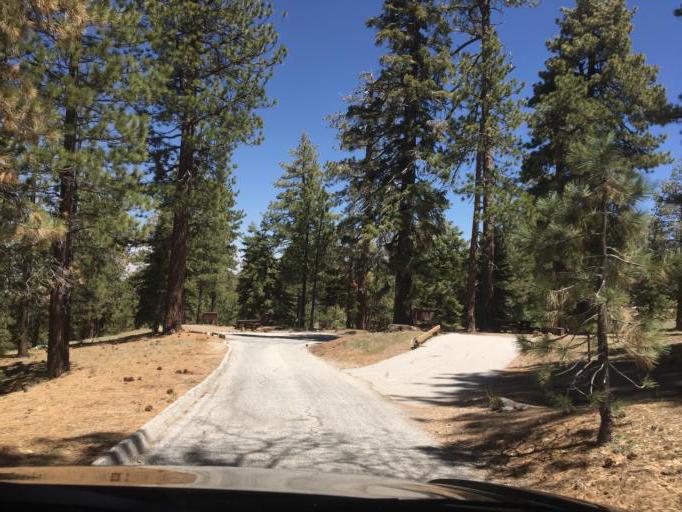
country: US
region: California
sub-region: San Bernardino County
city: Pinon Hills
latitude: 34.3895
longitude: -117.6960
